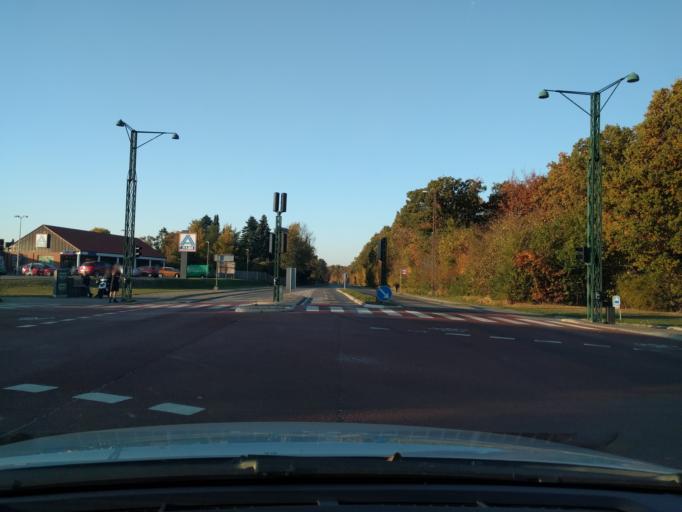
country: DK
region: Zealand
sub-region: Guldborgsund Kommune
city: Nykobing Falster
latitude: 54.7595
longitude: 11.8930
